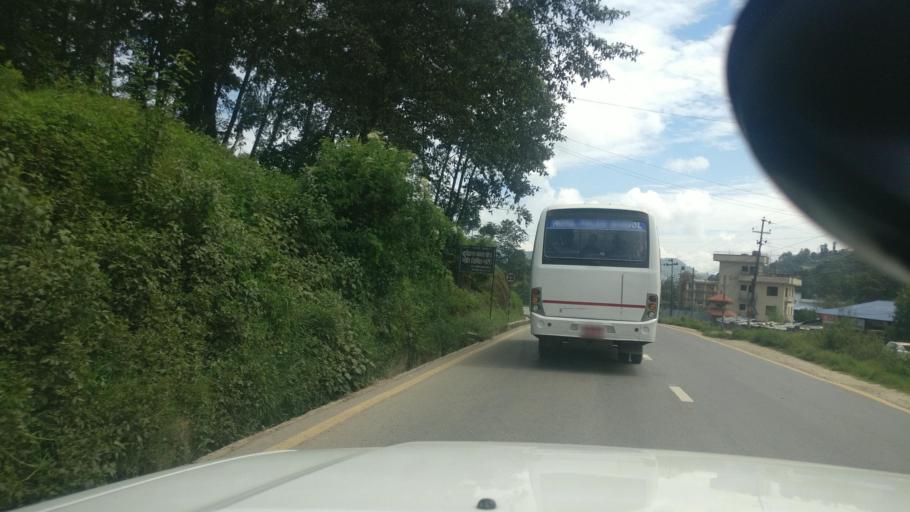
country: NP
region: Central Region
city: Banepa
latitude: 27.6316
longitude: 85.4969
